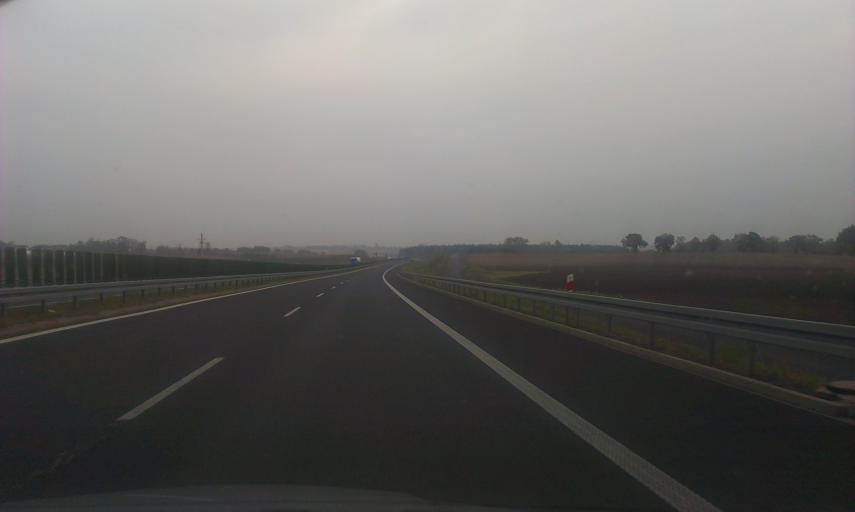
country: PL
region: Greater Poland Voivodeship
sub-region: Powiat poznanski
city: Rokietnica
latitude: 52.5048
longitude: 16.7707
